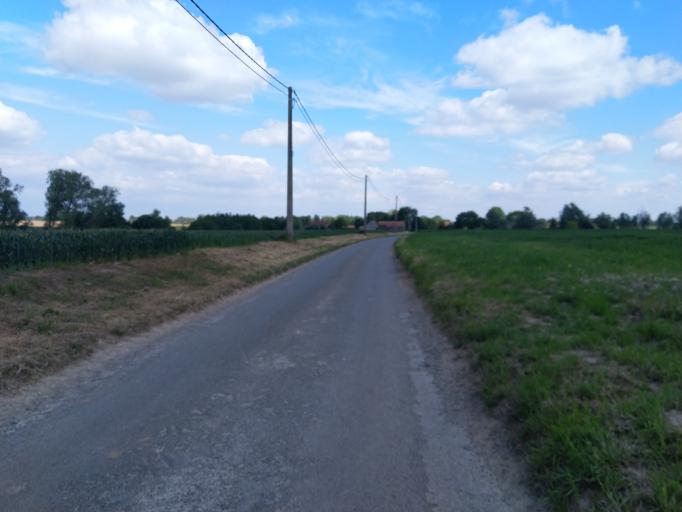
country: BE
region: Wallonia
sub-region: Province du Hainaut
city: Soignies
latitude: 50.5878
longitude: 4.0273
